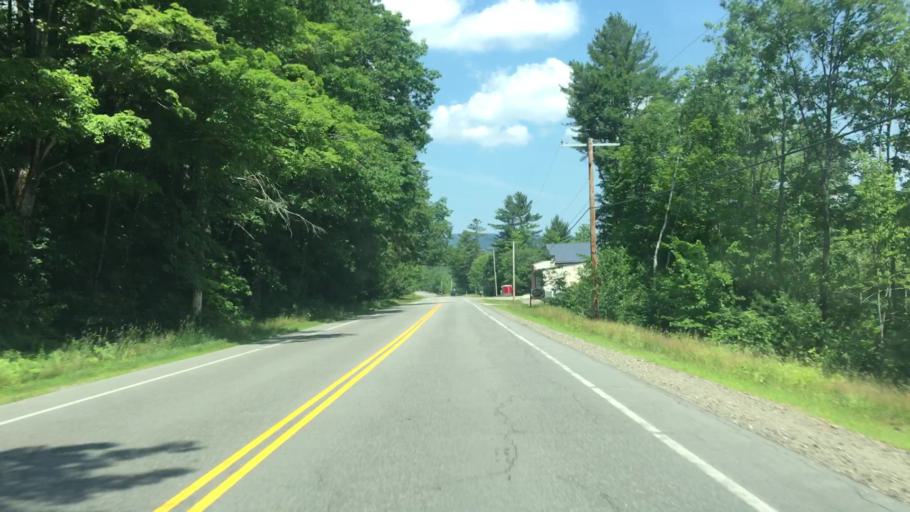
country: US
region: New Hampshire
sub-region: Sullivan County
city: Grantham
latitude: 43.4413
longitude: -72.1566
